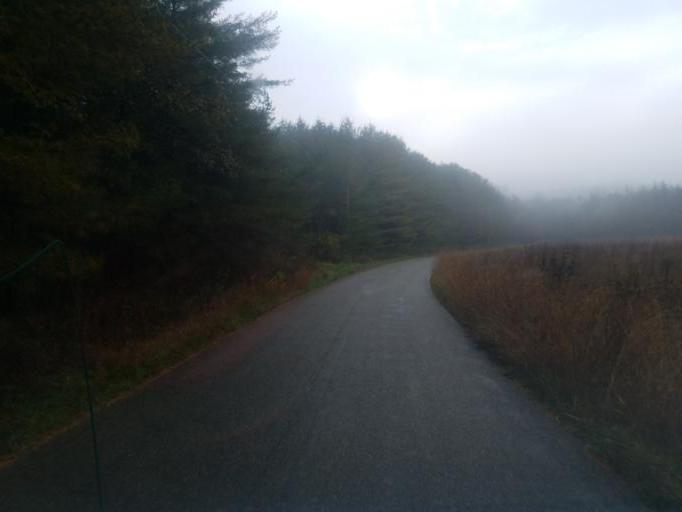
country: US
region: Ohio
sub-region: Athens County
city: Glouster
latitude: 39.4606
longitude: -81.9309
